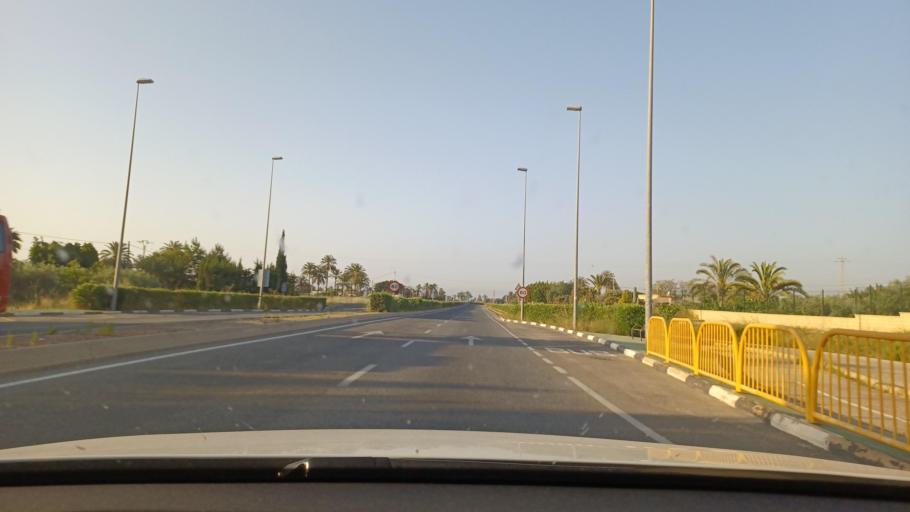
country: ES
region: Valencia
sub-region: Provincia de Alicante
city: Elche
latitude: 38.2396
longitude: -0.7003
